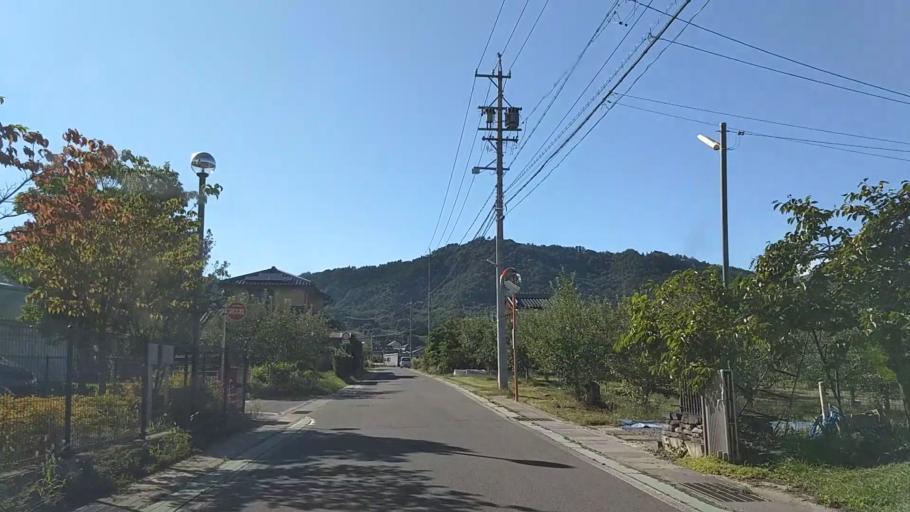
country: JP
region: Nagano
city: Nagano-shi
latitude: 36.6007
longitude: 138.1363
